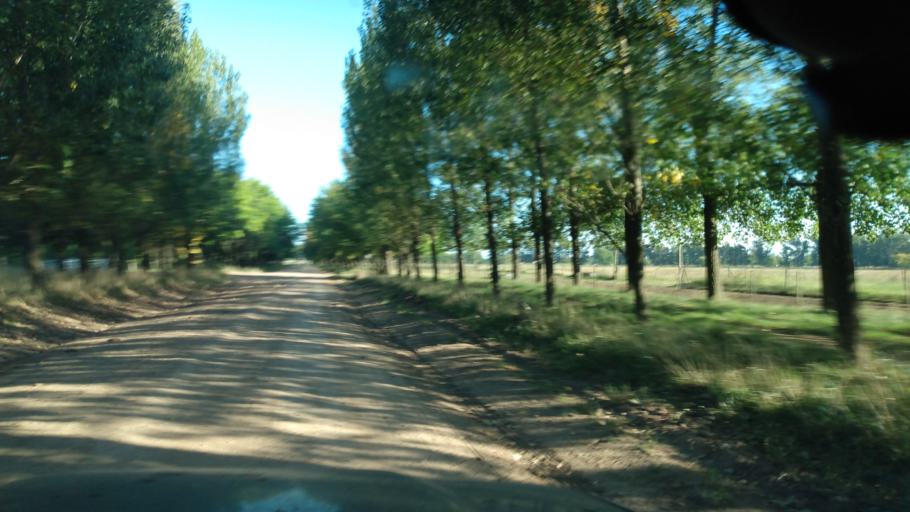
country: AR
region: Buenos Aires
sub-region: Partido de Lujan
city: Lujan
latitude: -34.5851
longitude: -59.0765
